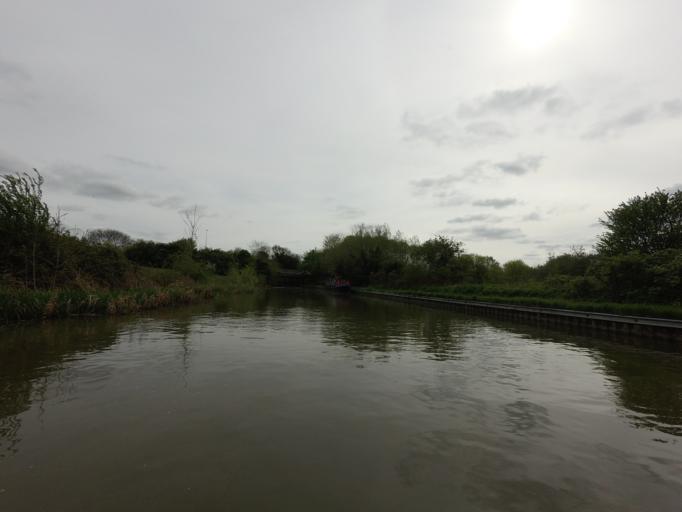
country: GB
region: England
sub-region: Milton Keynes
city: Bradwell
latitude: 52.0684
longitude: -0.7803
